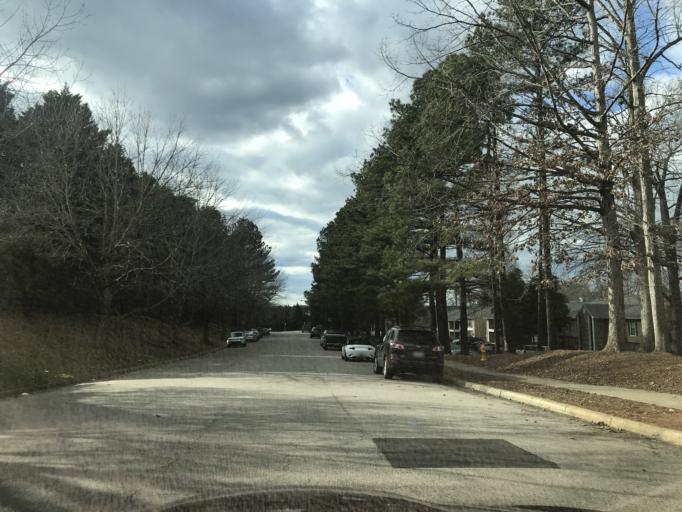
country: US
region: North Carolina
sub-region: Wake County
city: West Raleigh
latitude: 35.8605
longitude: -78.7152
